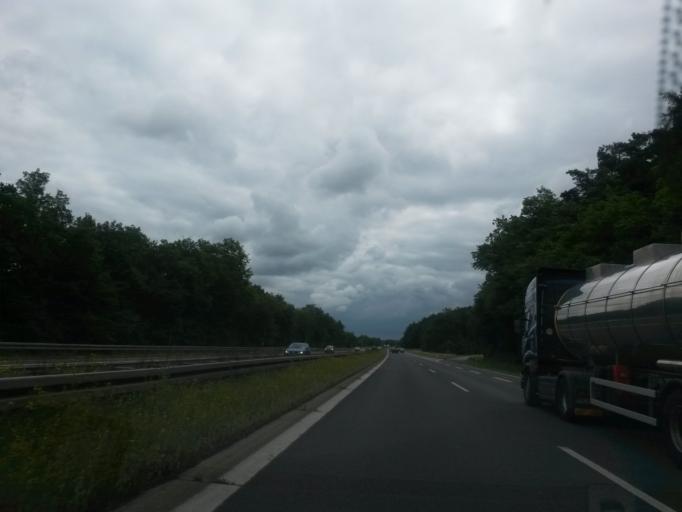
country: DE
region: Bavaria
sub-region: Regierungsbezirk Mittelfranken
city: Burghaslach
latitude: 49.7590
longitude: 10.5761
